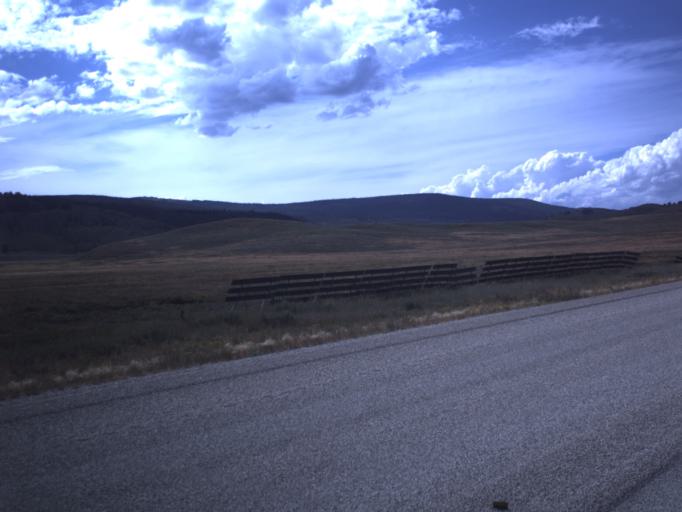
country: US
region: Utah
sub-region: Wasatch County
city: Heber
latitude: 40.2660
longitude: -111.2107
